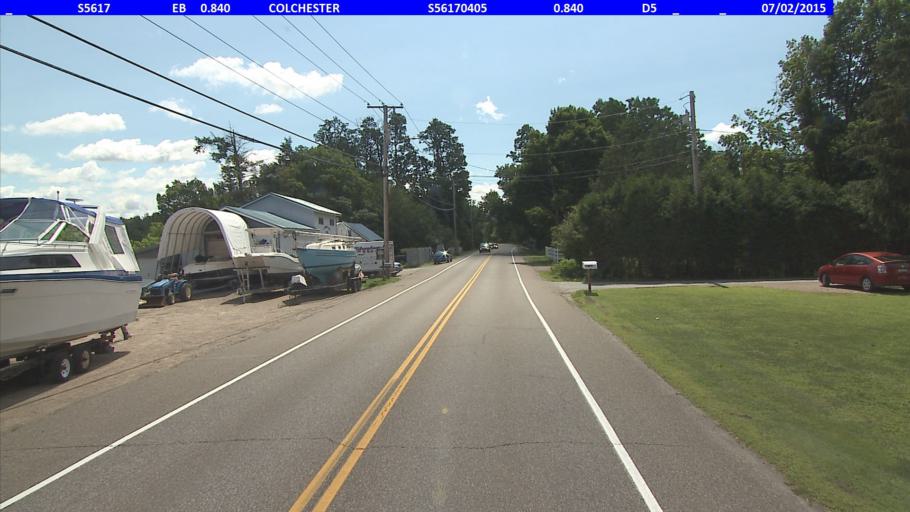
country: US
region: Vermont
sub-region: Chittenden County
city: Colchester
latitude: 44.5510
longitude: -73.1753
